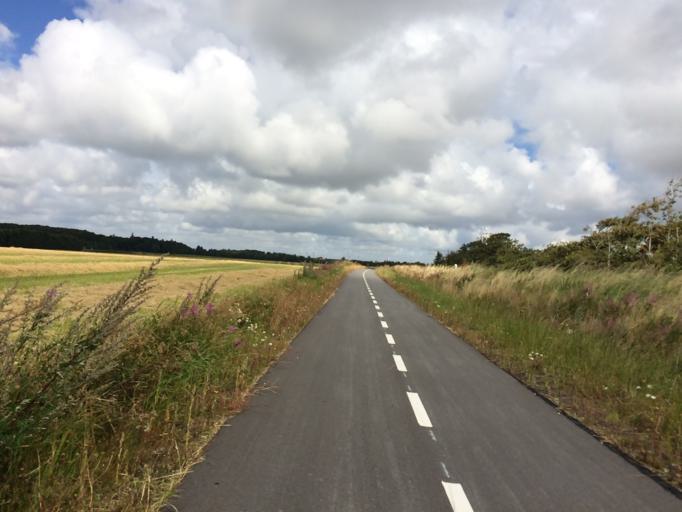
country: DK
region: Central Jutland
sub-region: Holstebro Kommune
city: Ulfborg
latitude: 56.3207
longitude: 8.3406
